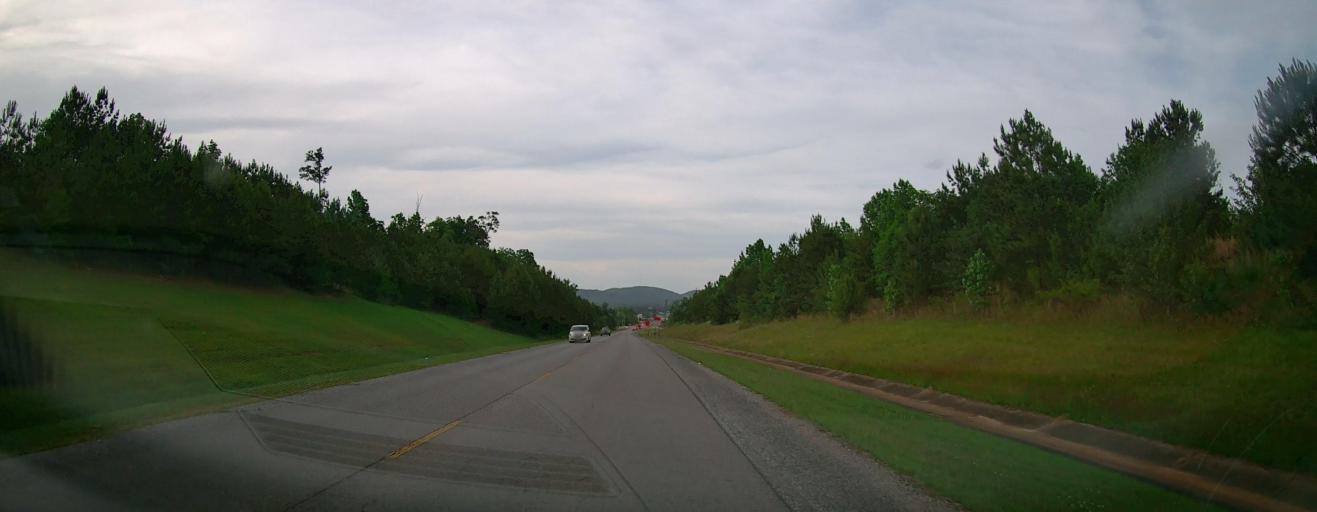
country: US
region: Alabama
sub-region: Calhoun County
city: Oxford
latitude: 33.5946
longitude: -85.7856
